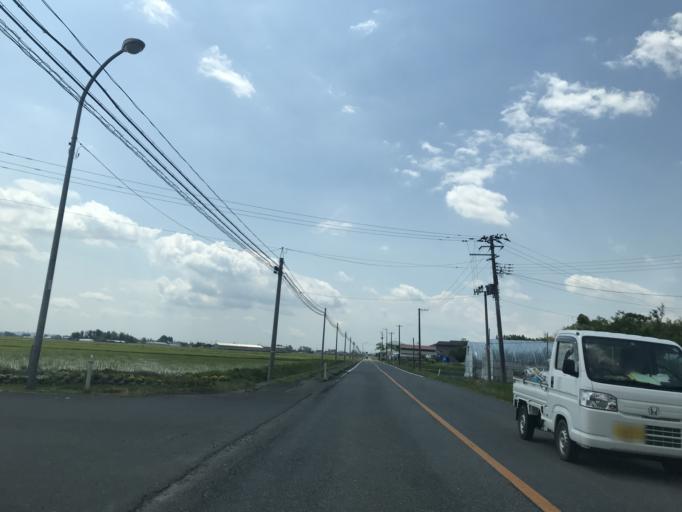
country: JP
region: Miyagi
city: Kogota
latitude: 38.6163
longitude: 141.0195
